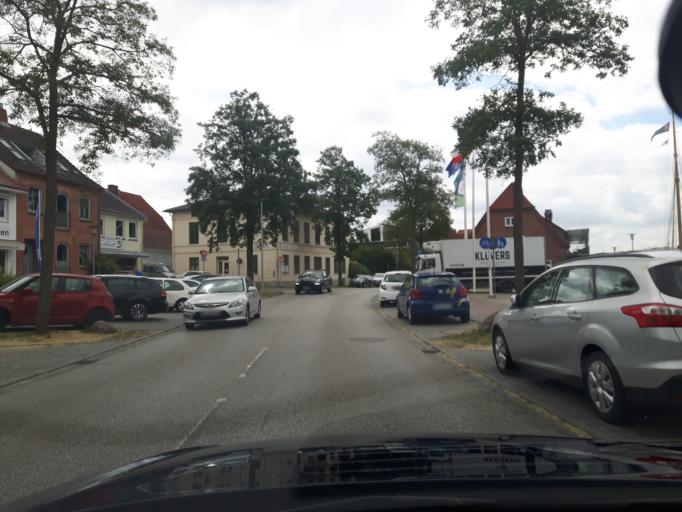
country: DE
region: Schleswig-Holstein
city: Neustadt in Holstein
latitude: 54.1064
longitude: 10.8112
